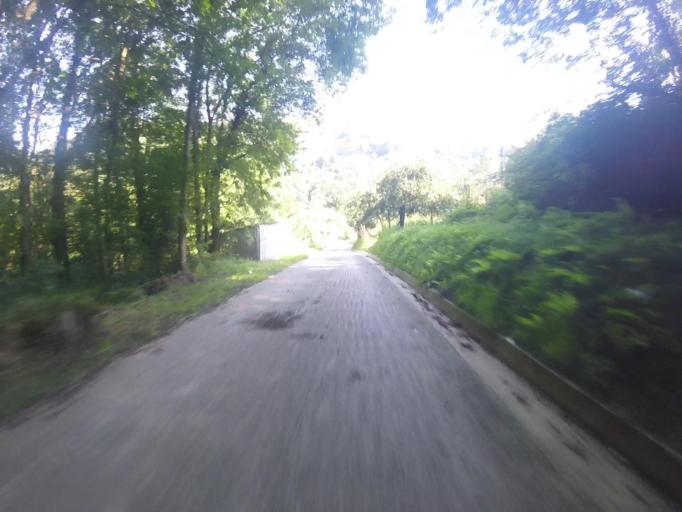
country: ES
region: Basque Country
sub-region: Provincia de Guipuzcoa
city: Astigarraga
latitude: 43.2552
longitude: -1.9392
